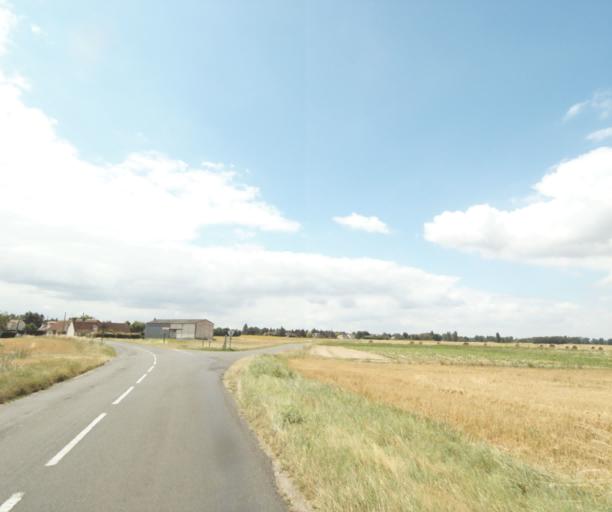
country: FR
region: Centre
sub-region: Departement du Loiret
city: Mardie
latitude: 47.8802
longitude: 2.0511
